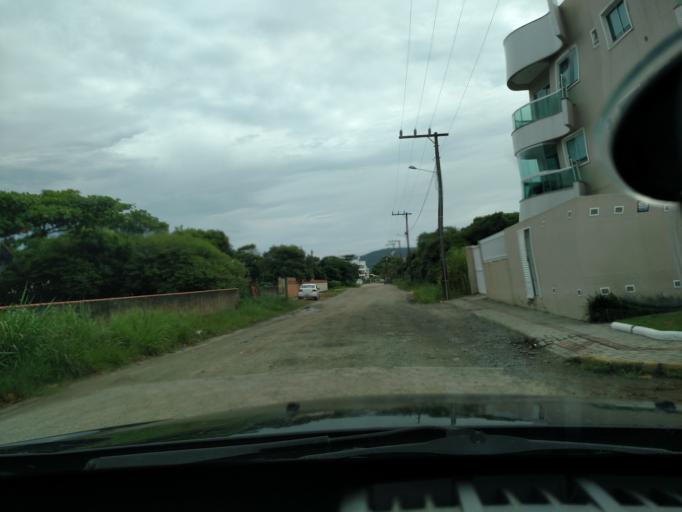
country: BR
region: Santa Catarina
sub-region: Porto Belo
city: Porto Belo
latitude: -27.1937
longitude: -48.5003
